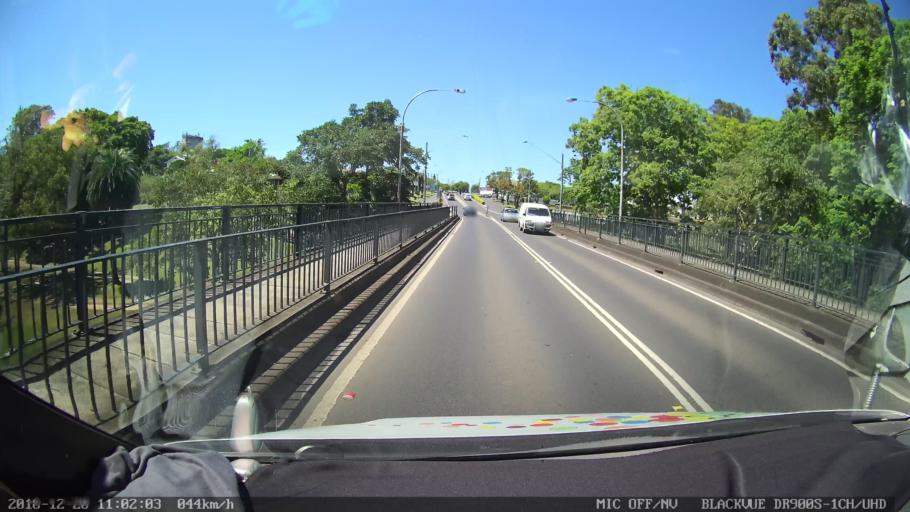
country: AU
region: New South Wales
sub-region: Richmond Valley
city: Casino
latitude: -28.8687
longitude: 153.0447
